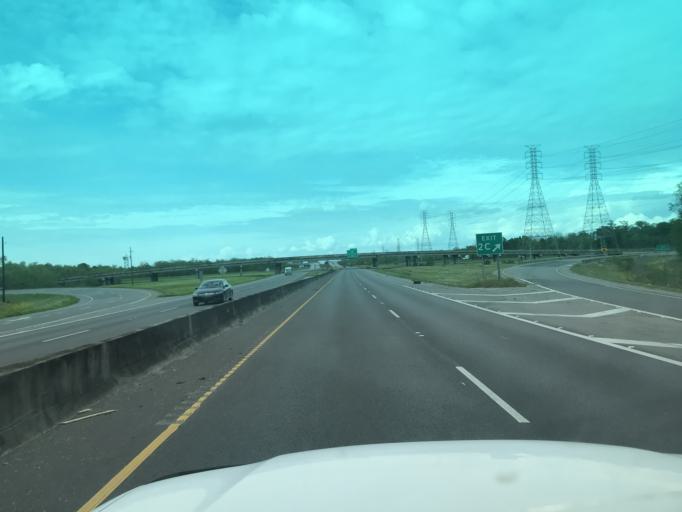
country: US
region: Louisiana
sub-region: Saint Bernard Parish
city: Chalmette
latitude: 30.0151
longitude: -89.9396
